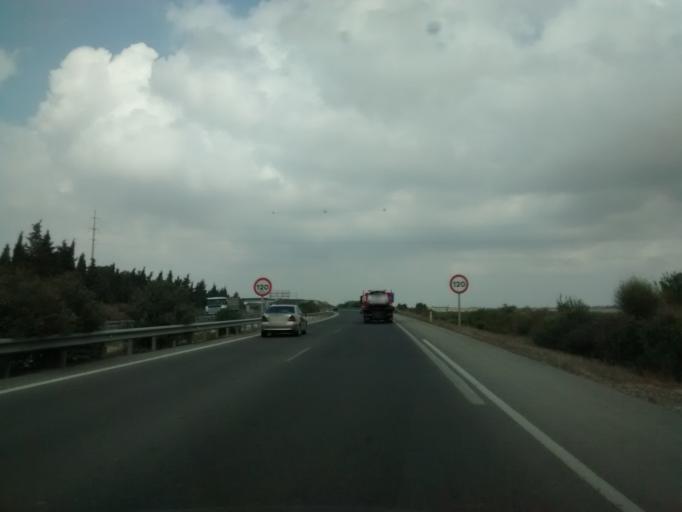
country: ES
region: Andalusia
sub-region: Provincia de Cadiz
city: Conil de la Frontera
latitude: 36.3501
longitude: -6.0663
